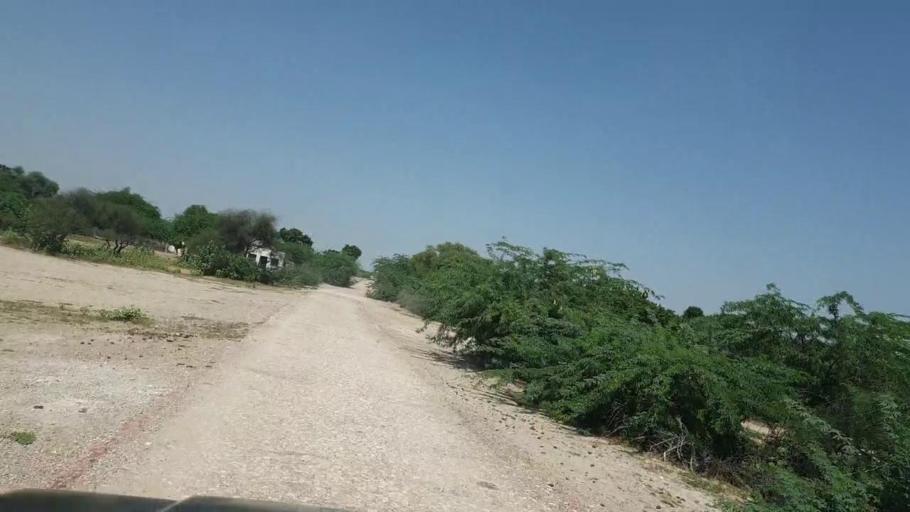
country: PK
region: Sindh
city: Chor
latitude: 25.3759
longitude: 70.3154
